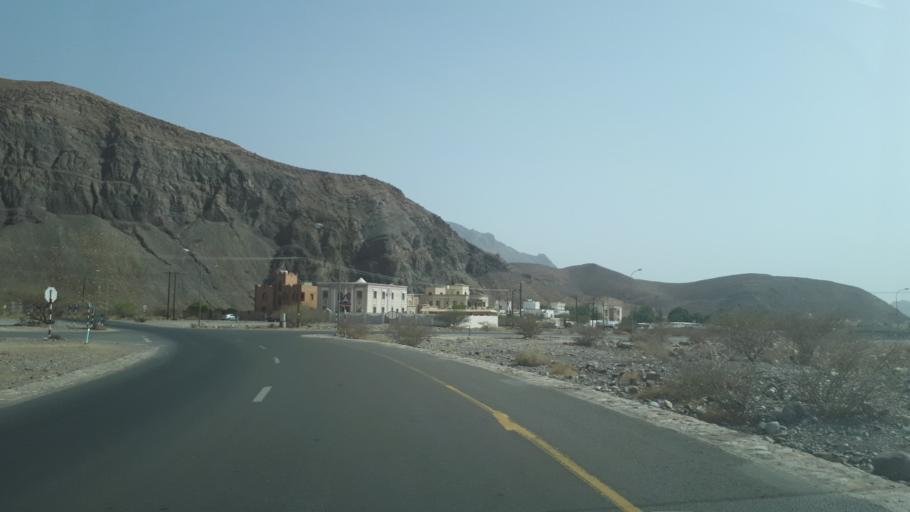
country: OM
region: Muhafazat ad Dakhiliyah
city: Bahla'
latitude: 23.2083
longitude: 56.9554
